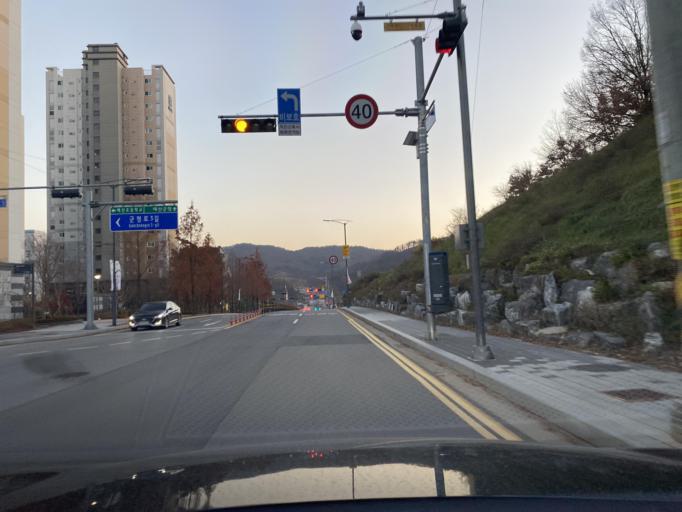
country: KR
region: Chungcheongnam-do
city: Yesan
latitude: 36.6830
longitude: 126.8436
